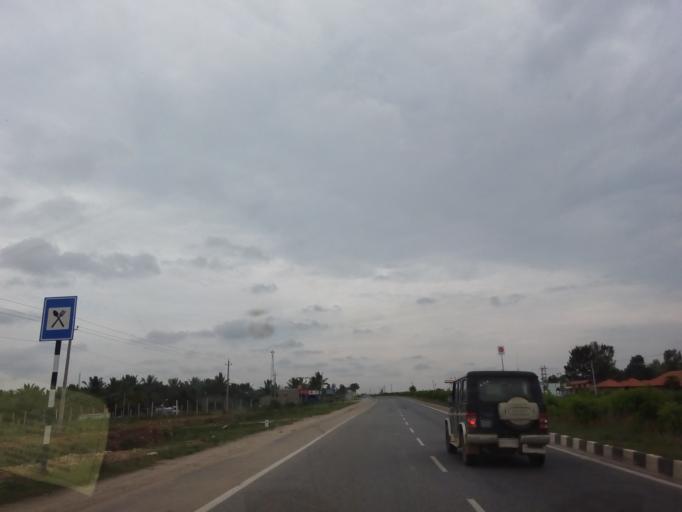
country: IN
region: Karnataka
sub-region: Hassan
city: Channarayapatna
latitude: 12.9615
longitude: 76.3302
